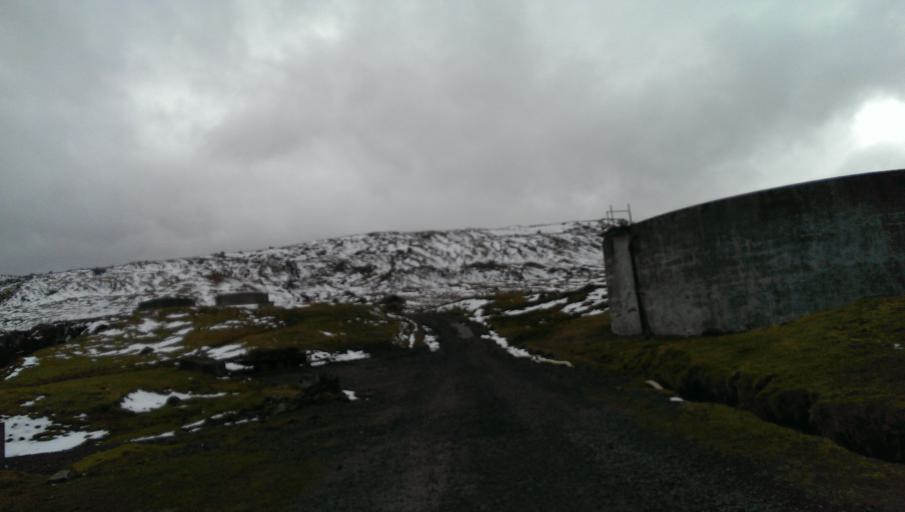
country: FO
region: Streymoy
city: Hoyvik
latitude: 62.0332
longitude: -6.8036
